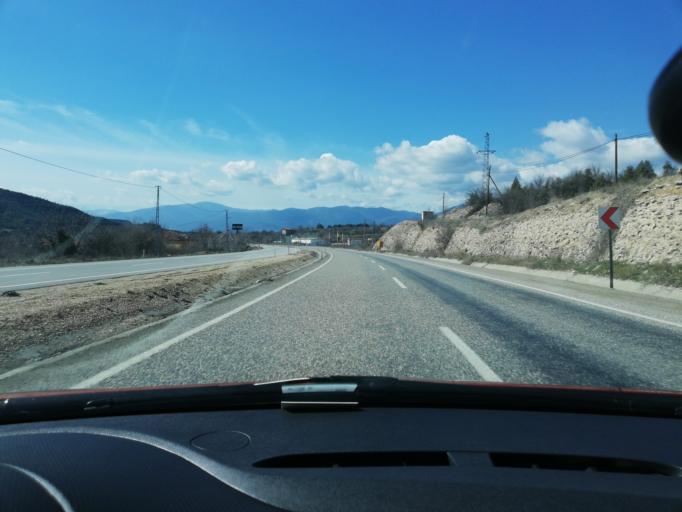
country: TR
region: Karabuk
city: Safranbolu
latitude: 41.2183
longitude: 32.7470
